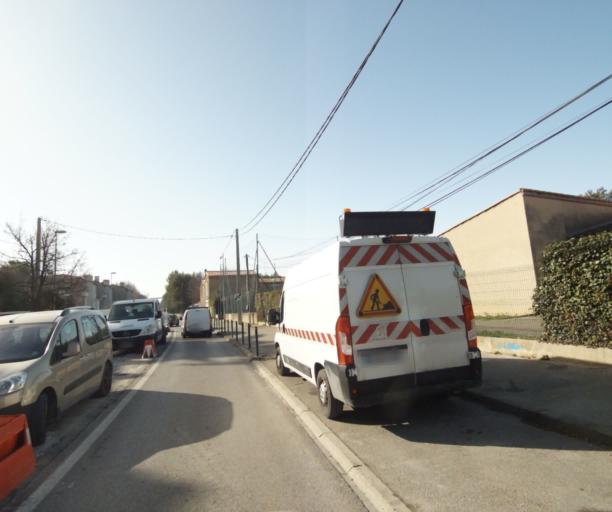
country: FR
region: Provence-Alpes-Cote d'Azur
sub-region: Departement des Bouches-du-Rhone
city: Aix-en-Provence
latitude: 43.5411
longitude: 5.4540
